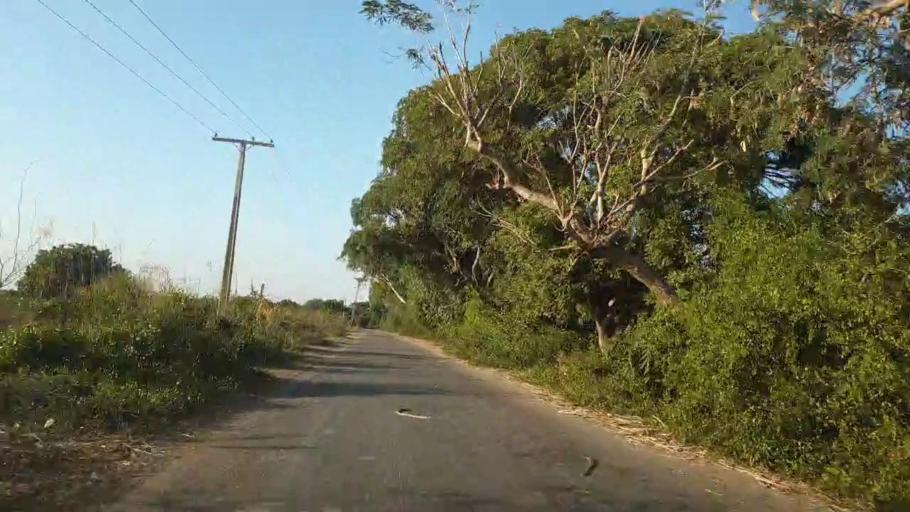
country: PK
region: Sindh
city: Mirpur Khas
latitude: 25.6551
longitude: 69.0970
